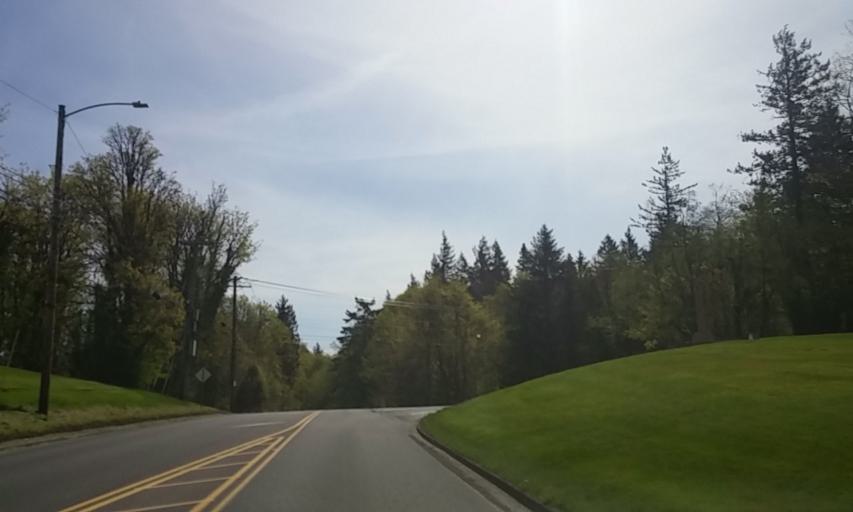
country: US
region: Oregon
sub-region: Washington County
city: West Haven-Sylvan
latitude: 45.5192
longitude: -122.7344
